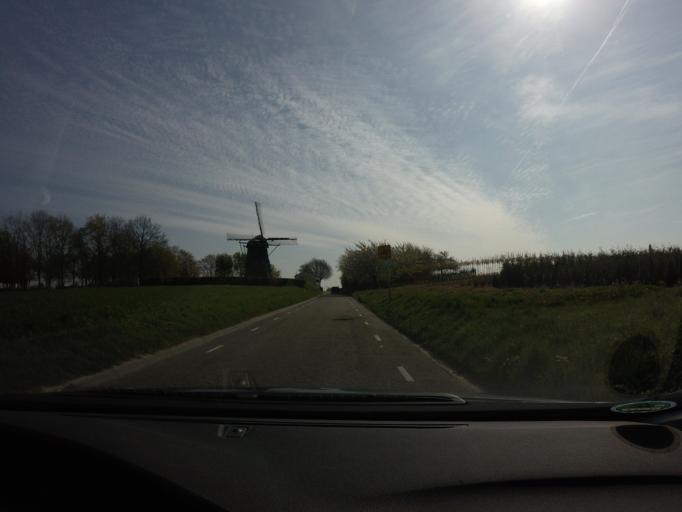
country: NL
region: Limburg
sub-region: Valkenburg aan de Geul
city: Sibbe
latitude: 50.8412
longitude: 5.8010
